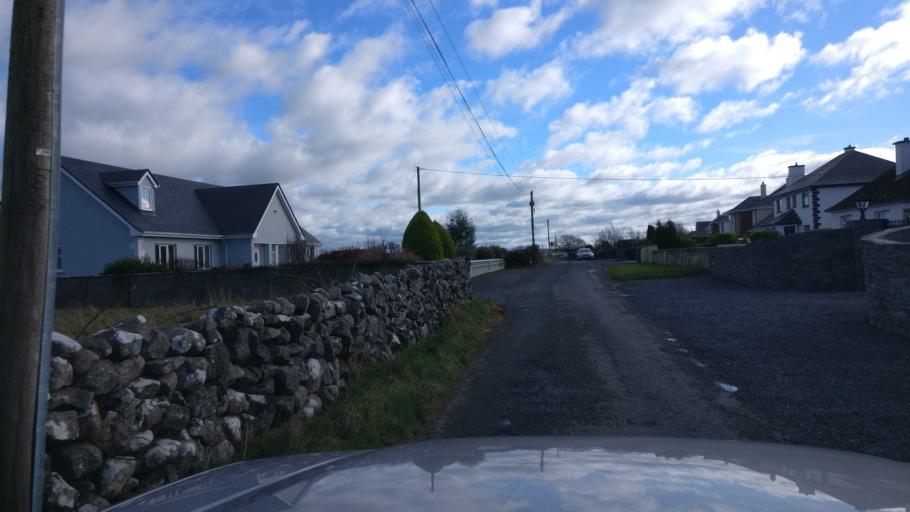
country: IE
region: Connaught
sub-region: County Galway
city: Oranmore
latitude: 53.2785
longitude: -8.8914
